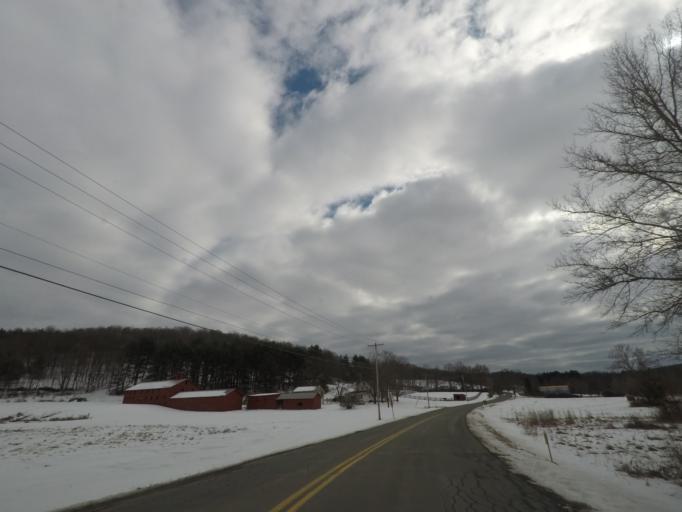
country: US
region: New York
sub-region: Rensselaer County
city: Hoosick Falls
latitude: 42.8989
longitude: -73.4223
